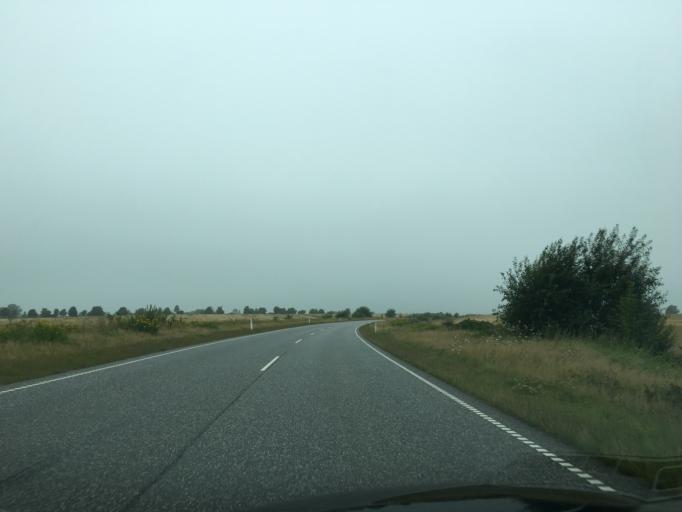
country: DK
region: South Denmark
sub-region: Kolding Kommune
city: Kolding
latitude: 55.5472
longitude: 9.4531
